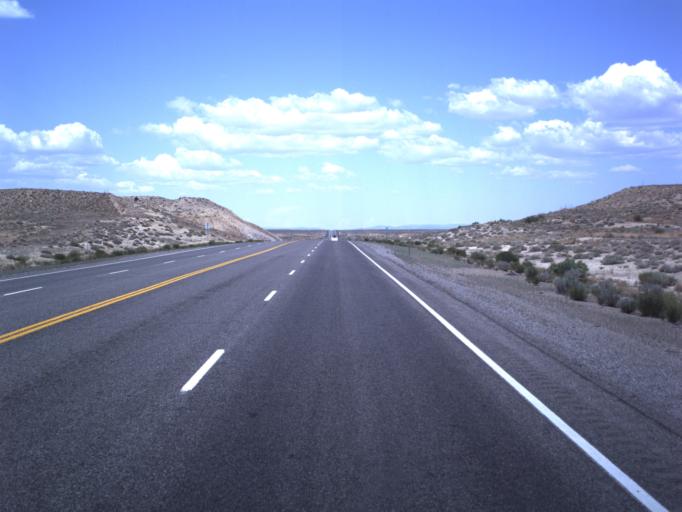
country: US
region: Utah
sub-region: Emery County
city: Huntington
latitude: 39.3759
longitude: -110.9130
